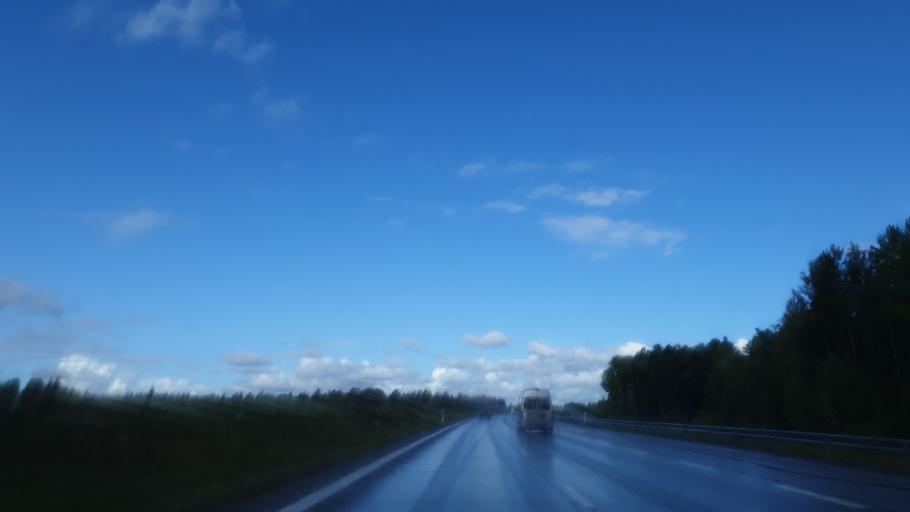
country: SE
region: Uppsala
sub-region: Osthammars Kommun
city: Bjorklinge
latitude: 60.0084
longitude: 17.6261
